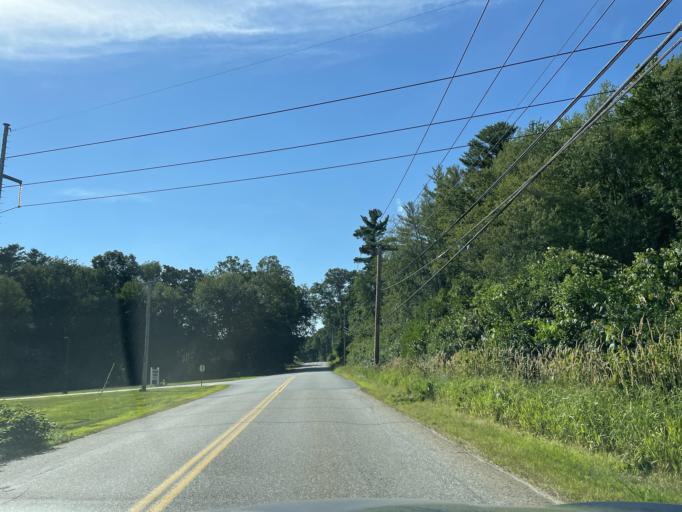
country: US
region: Massachusetts
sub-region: Worcester County
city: Charlton
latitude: 42.1333
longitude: -71.9386
